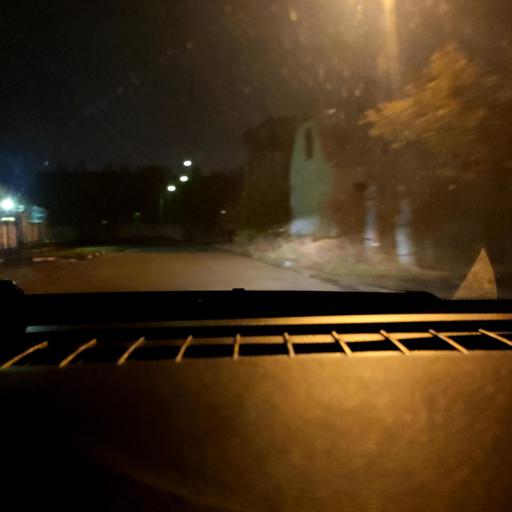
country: RU
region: Voronezj
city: Voronezh
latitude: 51.6284
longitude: 39.1675
